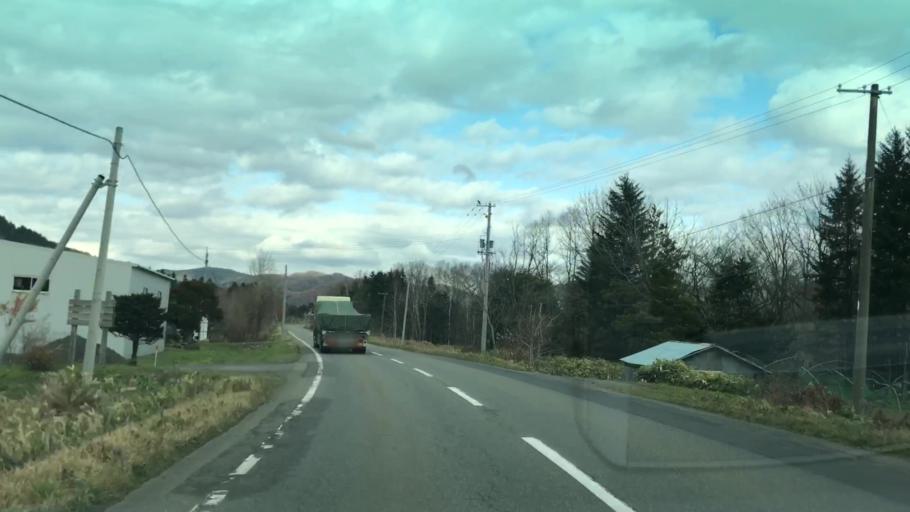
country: JP
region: Hokkaido
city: Shimo-furano
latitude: 42.8624
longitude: 142.4223
